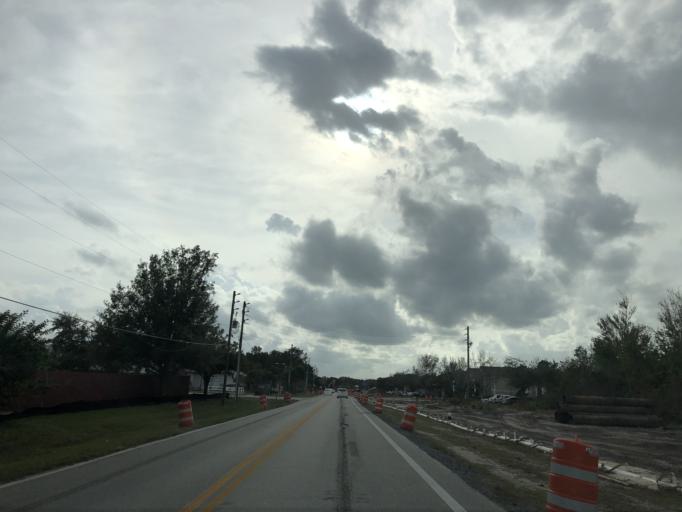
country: US
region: Florida
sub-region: Osceola County
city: Buenaventura Lakes
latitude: 28.2815
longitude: -81.3553
